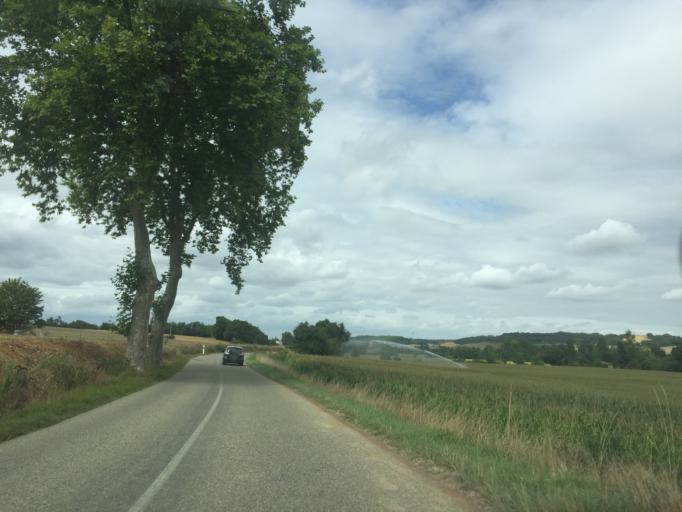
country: FR
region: Midi-Pyrenees
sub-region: Departement du Gers
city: Jegun
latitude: 43.6774
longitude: 0.3916
